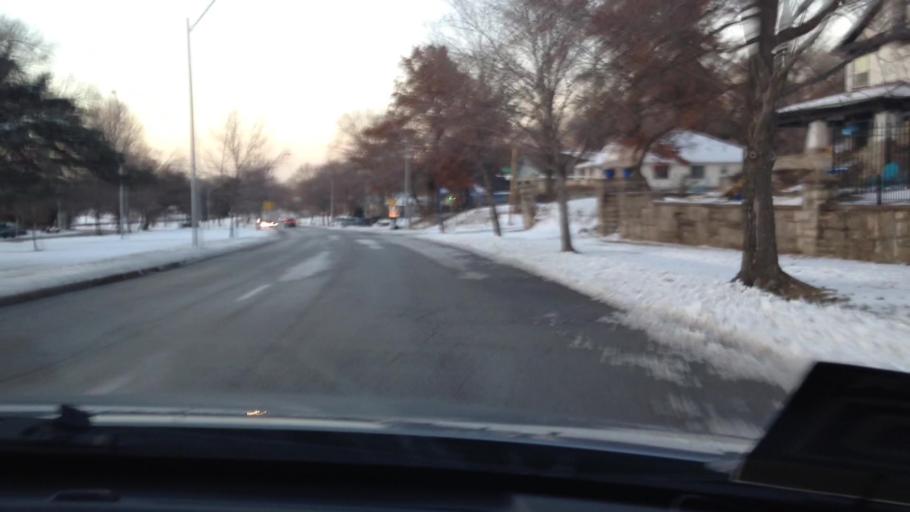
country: US
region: Kansas
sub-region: Johnson County
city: Mission Hills
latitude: 39.0013
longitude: -94.5625
